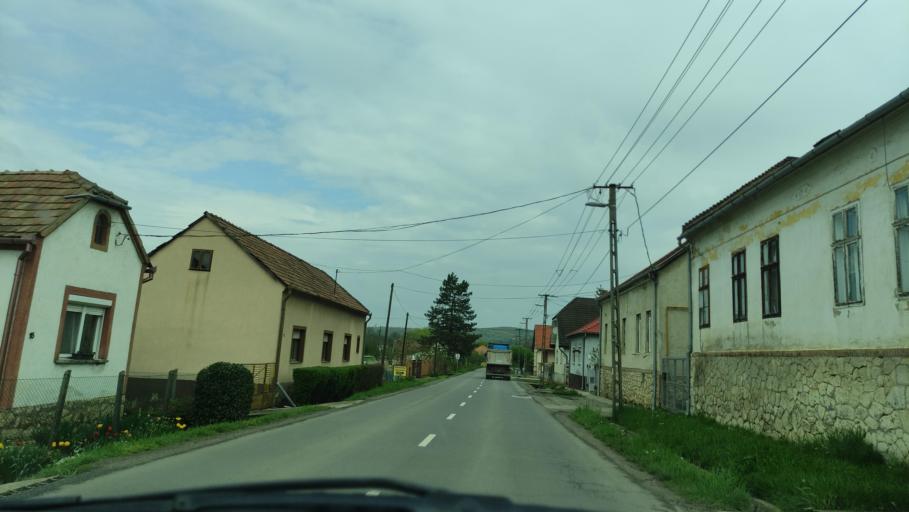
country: HU
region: Baranya
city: Komlo
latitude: 46.2133
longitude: 18.2433
